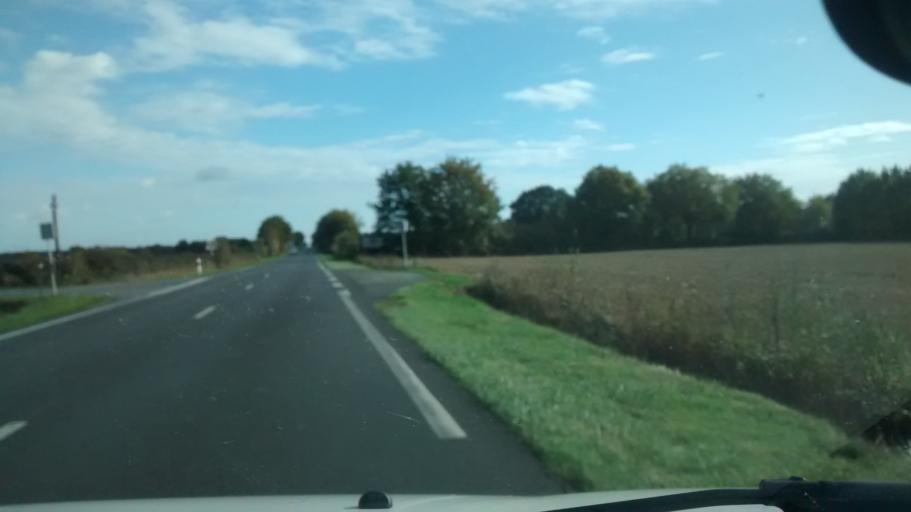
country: FR
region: Pays de la Loire
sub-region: Departement de la Loire-Atlantique
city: Soudan
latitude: 47.7447
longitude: -1.2507
